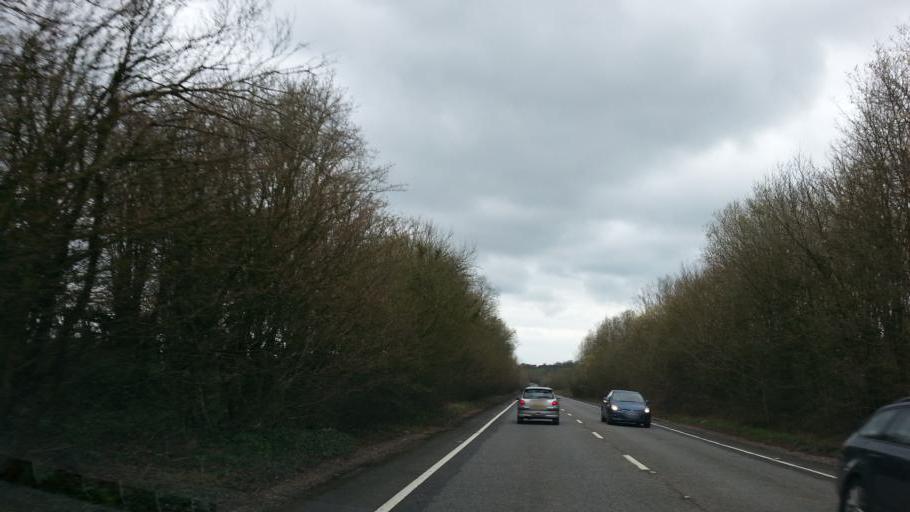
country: GB
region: England
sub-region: Devon
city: Barnstaple
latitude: 51.0625
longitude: -3.9853
